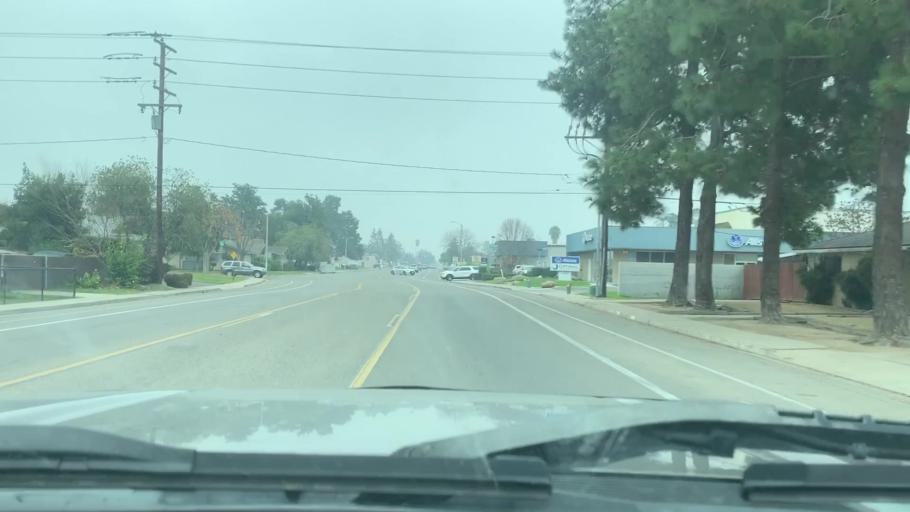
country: US
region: California
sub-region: Tulare County
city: Visalia
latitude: 36.3057
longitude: -119.3186
